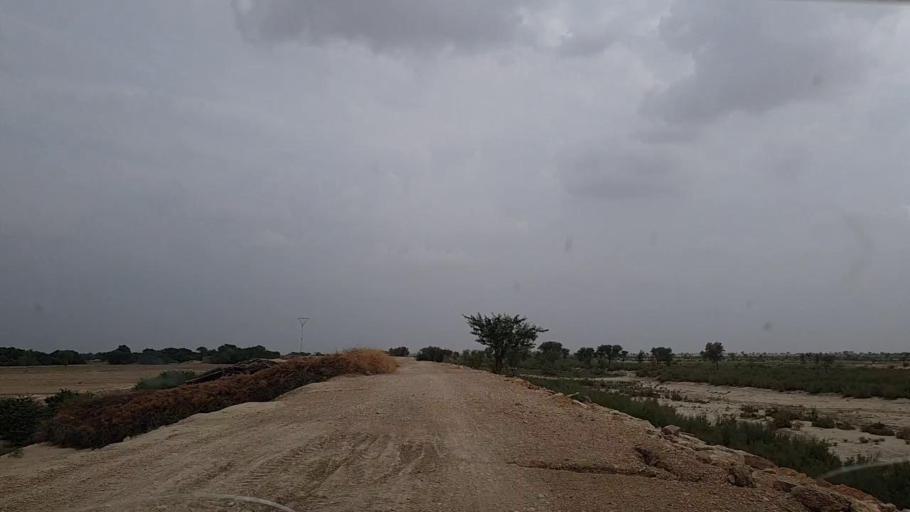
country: PK
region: Sindh
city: Johi
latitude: 26.7251
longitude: 67.5780
